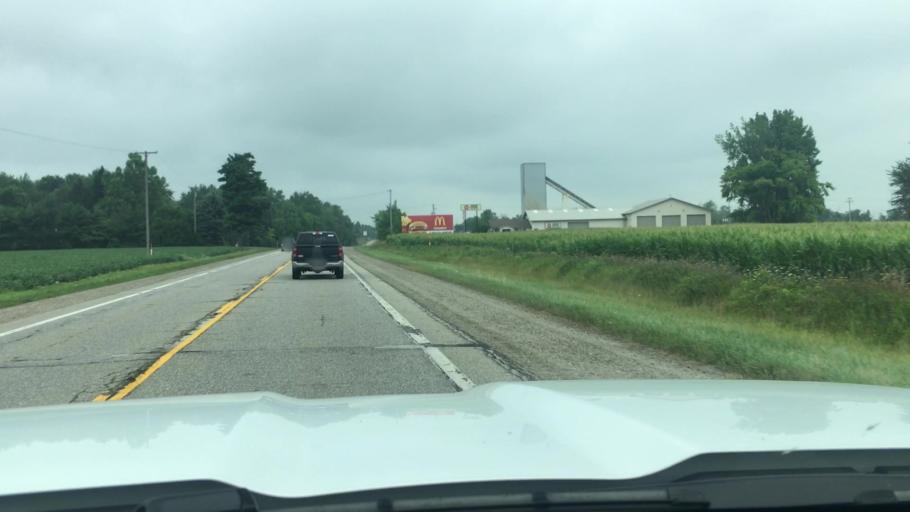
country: US
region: Michigan
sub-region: Sanilac County
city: Marlette
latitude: 43.2464
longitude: -83.0790
